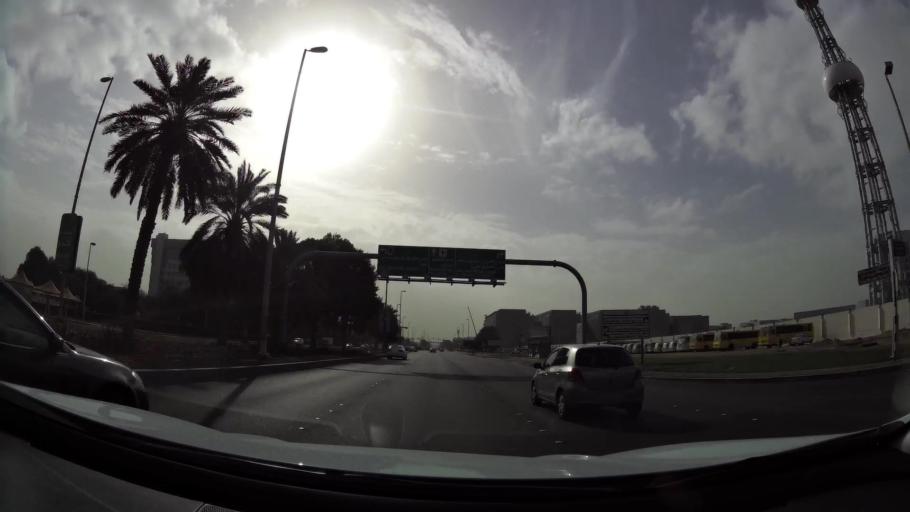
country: AE
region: Abu Dhabi
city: Abu Dhabi
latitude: 24.4529
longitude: 54.3949
